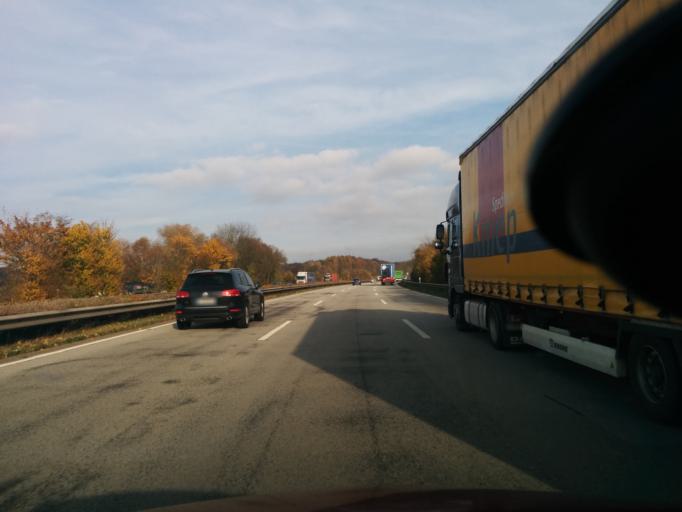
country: DE
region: Rheinland-Pfalz
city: Weitersburg
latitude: 50.4230
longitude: 7.6160
